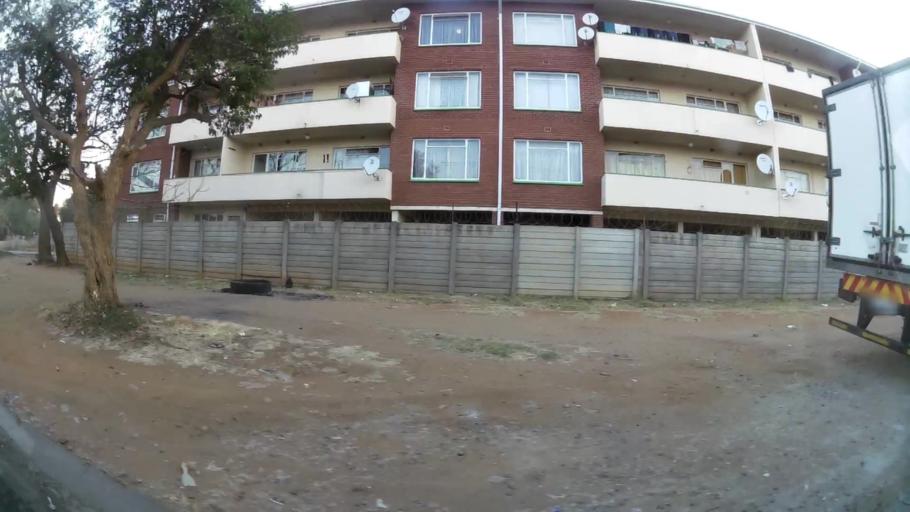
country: ZA
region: North-West
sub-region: Bojanala Platinum District Municipality
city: Rustenburg
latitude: -25.6650
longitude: 27.2496
